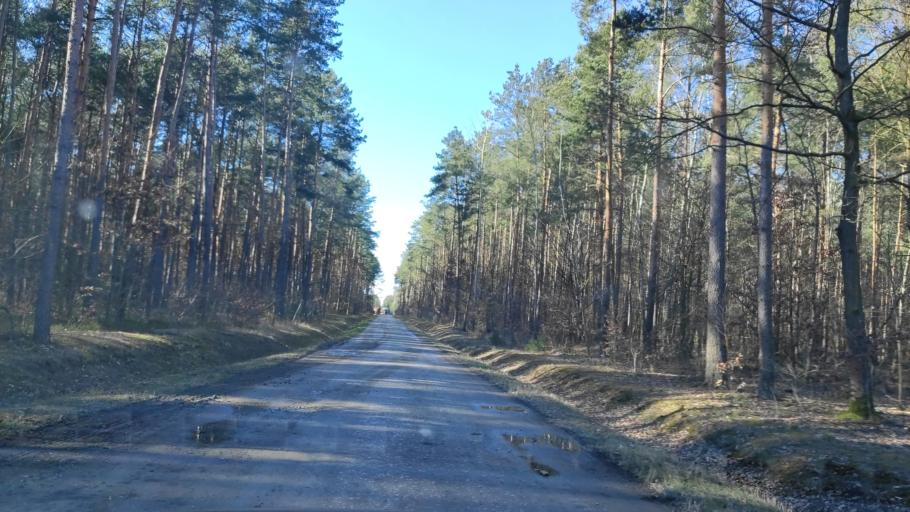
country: PL
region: Masovian Voivodeship
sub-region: Powiat radomski
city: Jedlnia-Letnisko
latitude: 51.4620
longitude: 21.3247
